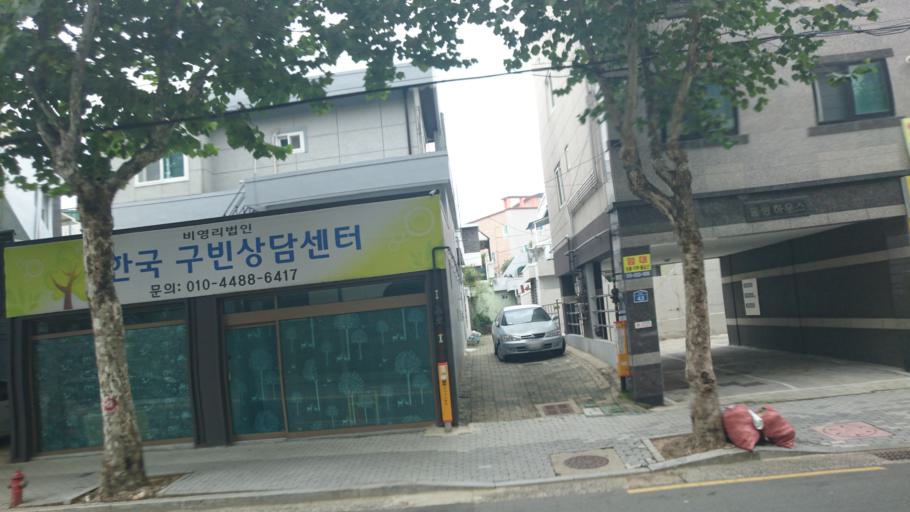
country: KR
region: Daegu
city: Daegu
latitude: 35.8815
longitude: 128.6466
